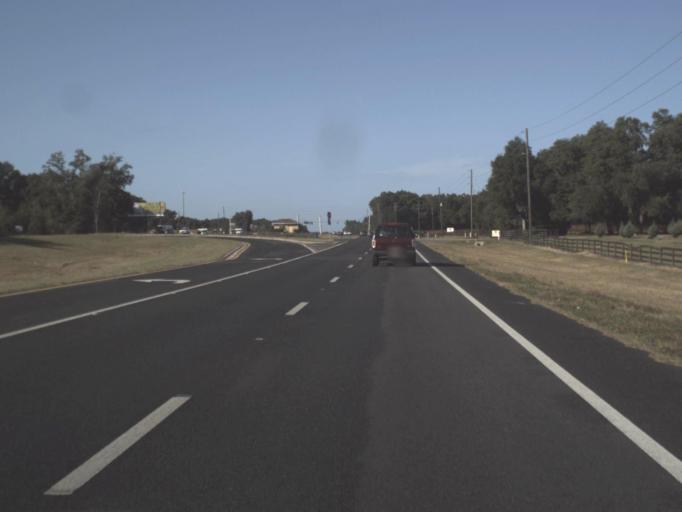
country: US
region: Florida
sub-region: Marion County
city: Belleview
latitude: 29.0260
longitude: -82.1151
